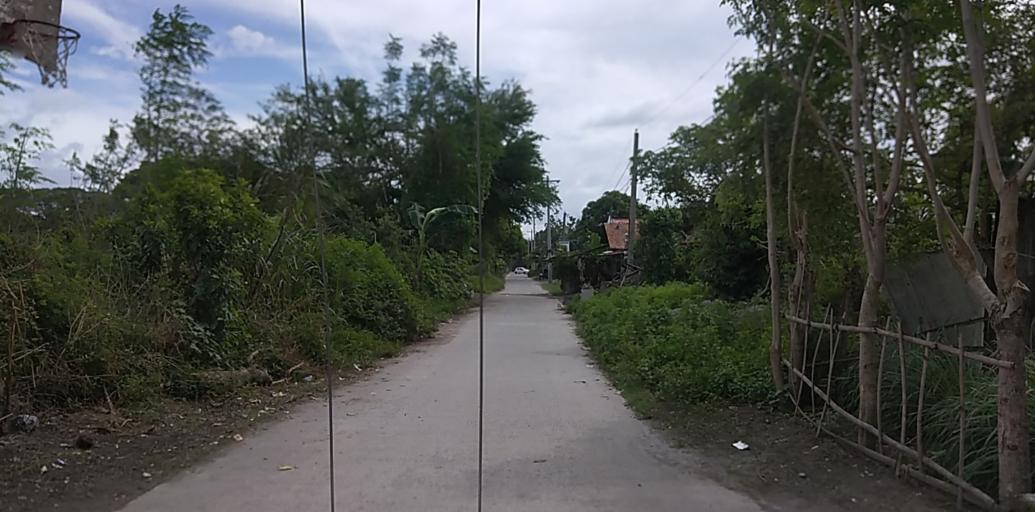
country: PH
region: Central Luzon
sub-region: Province of Pampanga
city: Manibaug Pasig
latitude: 15.1098
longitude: 120.5584
